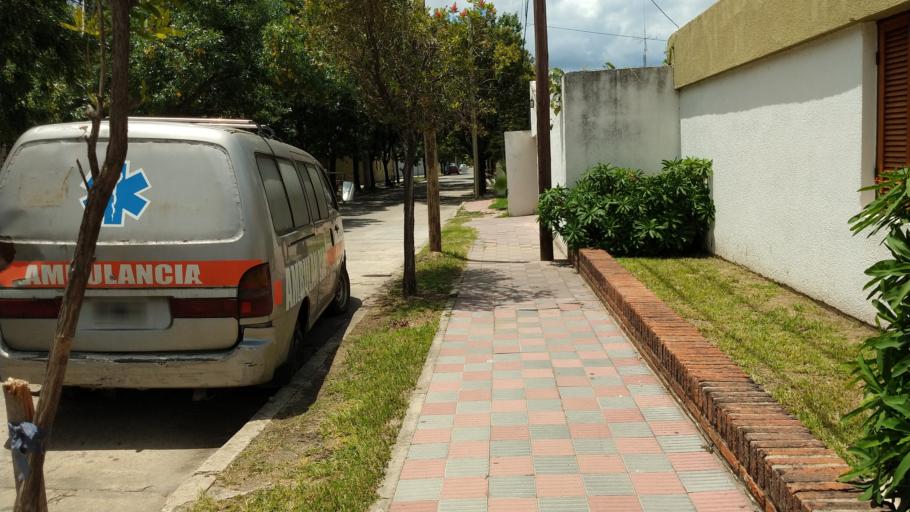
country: AR
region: Cordoba
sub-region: Departamento de Capital
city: Cordoba
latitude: -31.3648
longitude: -64.2304
